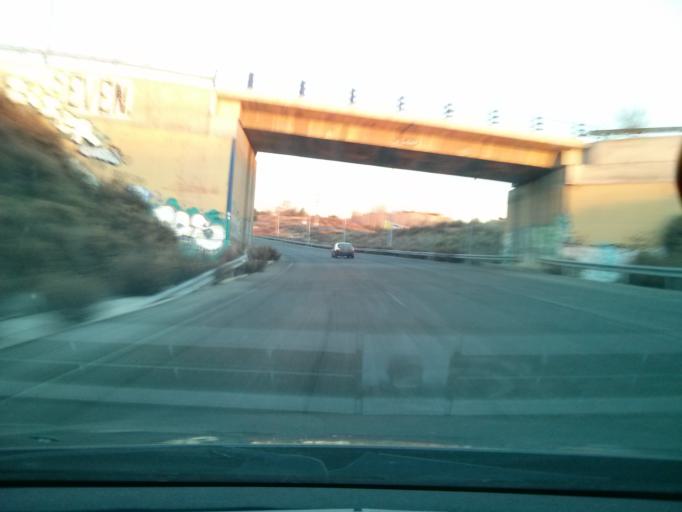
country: ES
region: Madrid
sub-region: Provincia de Madrid
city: Las Tablas
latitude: 40.5083
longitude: -3.6513
